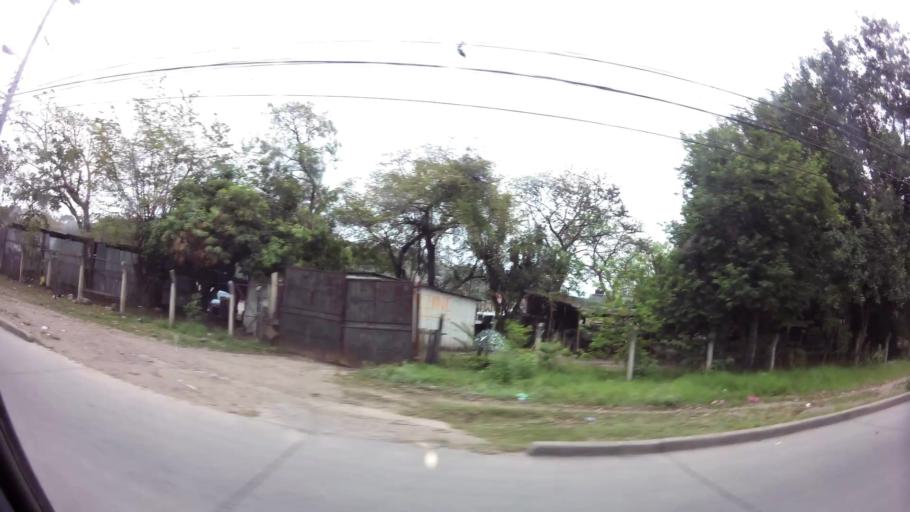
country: HN
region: Francisco Morazan
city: Tegucigalpa
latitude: 14.0658
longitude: -87.1988
